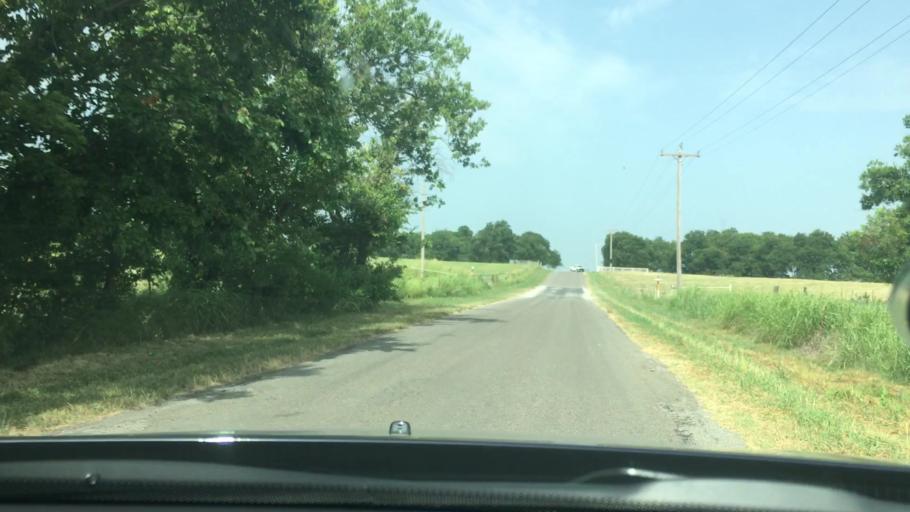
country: US
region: Oklahoma
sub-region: Garvin County
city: Pauls Valley
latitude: 34.7967
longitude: -97.1684
